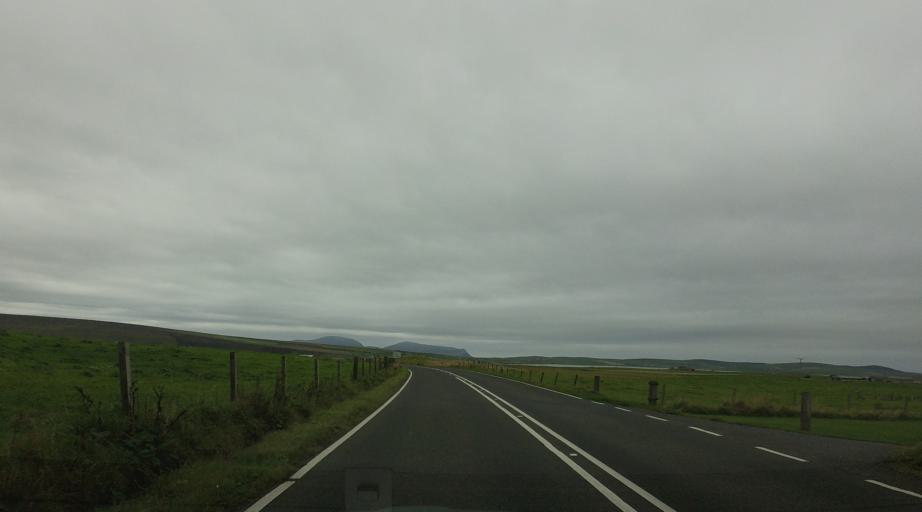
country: GB
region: Scotland
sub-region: Orkney Islands
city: Stromness
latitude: 59.0023
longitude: -3.1723
